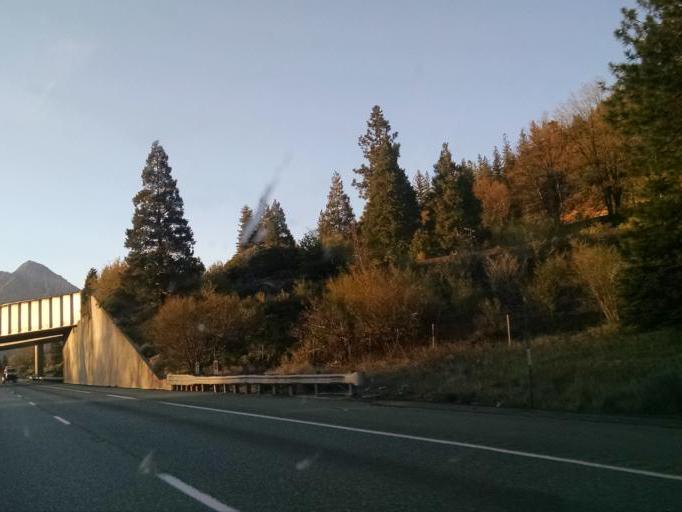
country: US
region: California
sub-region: Siskiyou County
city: Mount Shasta
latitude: 41.3297
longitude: -122.3307
